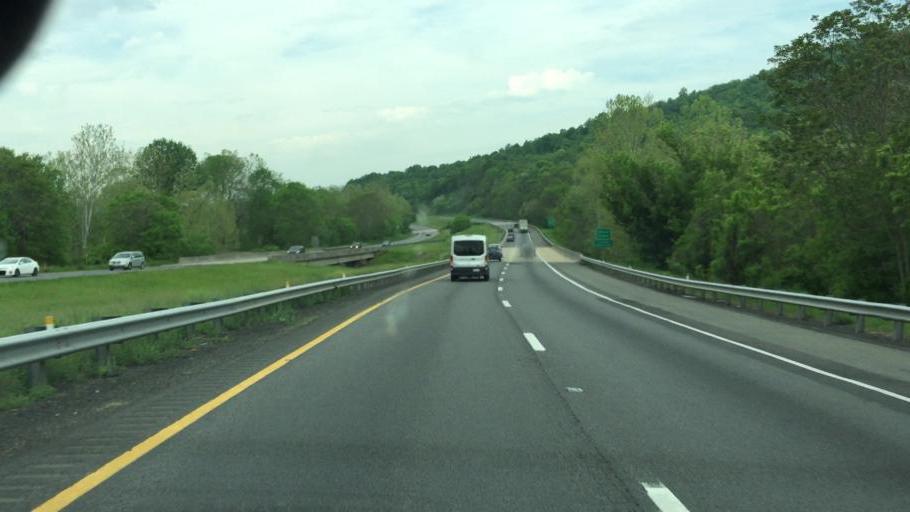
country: US
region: Virginia
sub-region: Fauquier County
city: Marshall
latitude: 38.9091
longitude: -77.9692
